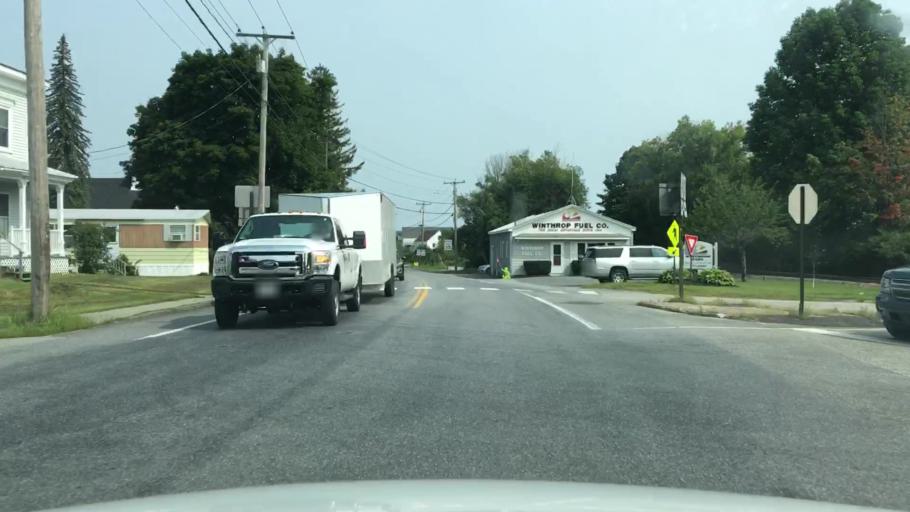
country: US
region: Maine
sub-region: Kennebec County
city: Winthrop
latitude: 44.3051
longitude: -69.9773
